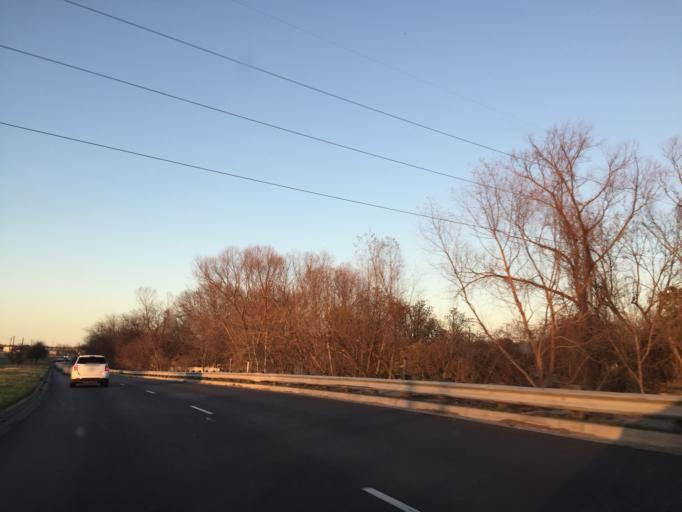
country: US
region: Texas
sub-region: Travis County
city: Pflugerville
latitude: 30.4075
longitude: -97.6356
